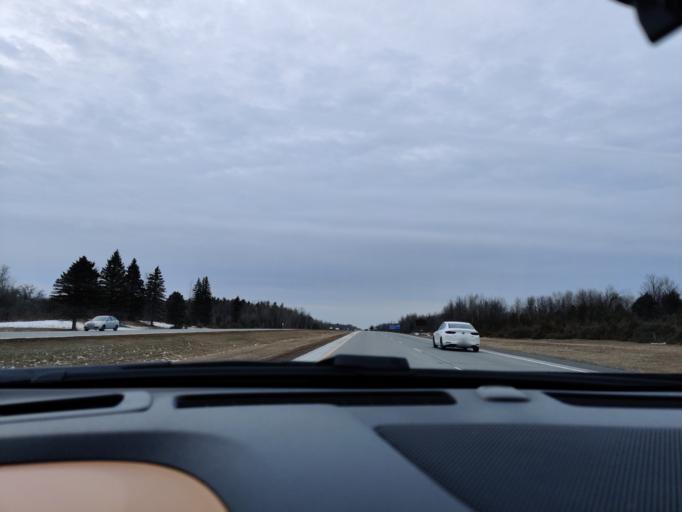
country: US
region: New York
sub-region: St. Lawrence County
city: Ogdensburg
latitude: 44.8258
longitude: -75.3815
